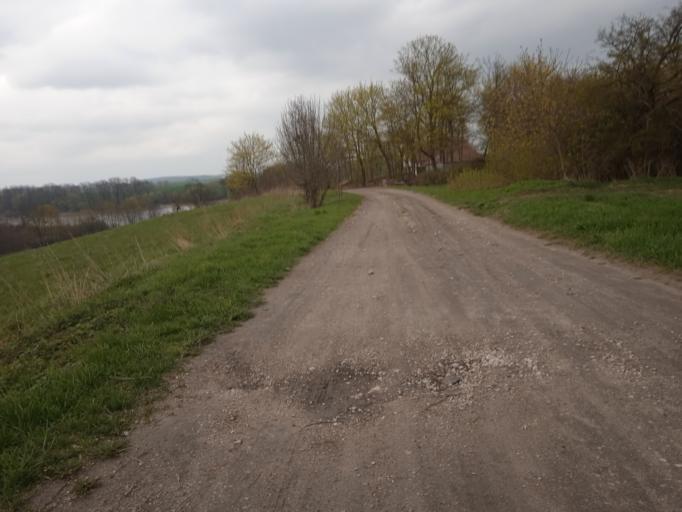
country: PL
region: Kujawsko-Pomorskie
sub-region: Powiat grudziadzki
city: Lasin
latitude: 53.5709
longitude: 19.0600
